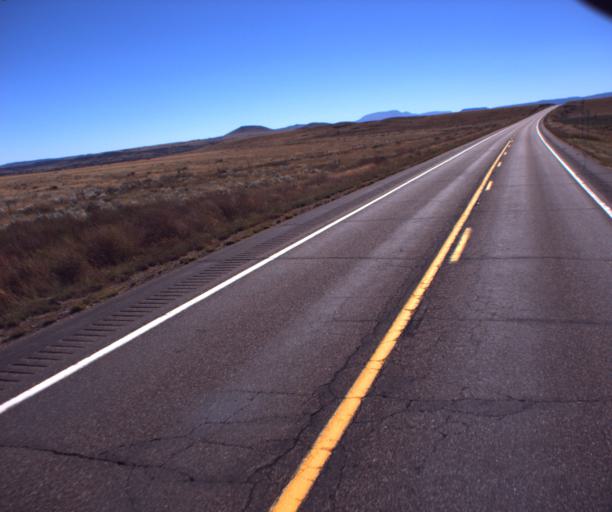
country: US
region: Arizona
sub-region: Apache County
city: Saint Johns
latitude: 34.3199
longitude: -109.3829
